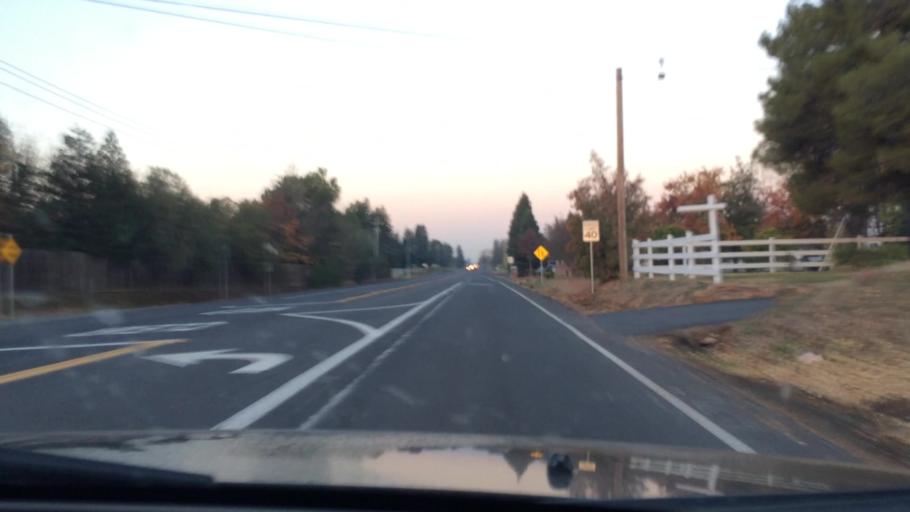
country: US
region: California
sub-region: Sacramento County
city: Vineyard
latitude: 38.4382
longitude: -121.3546
